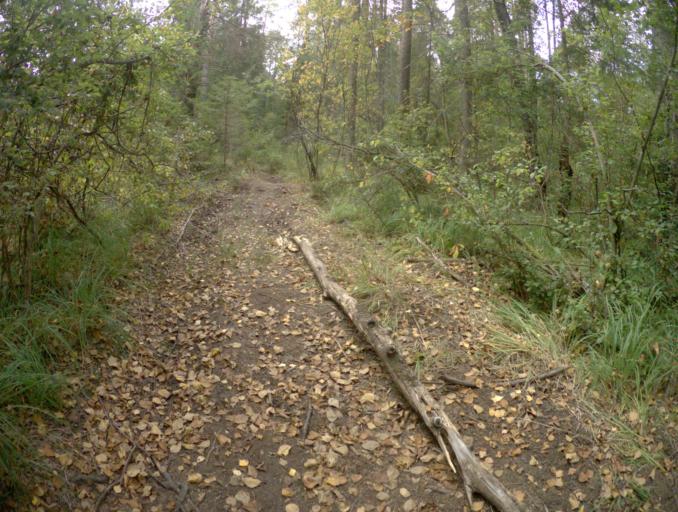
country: RU
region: Vladimir
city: Kommunar
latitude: 56.0317
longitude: 40.4928
